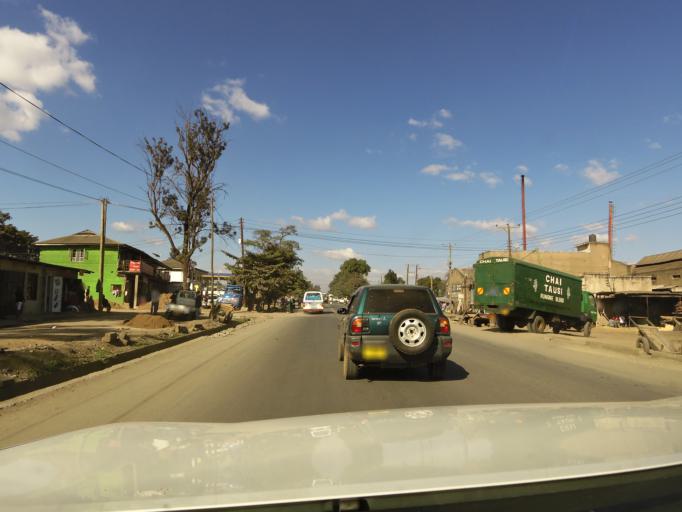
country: TZ
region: Arusha
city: Arusha
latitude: -3.3761
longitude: 36.6617
